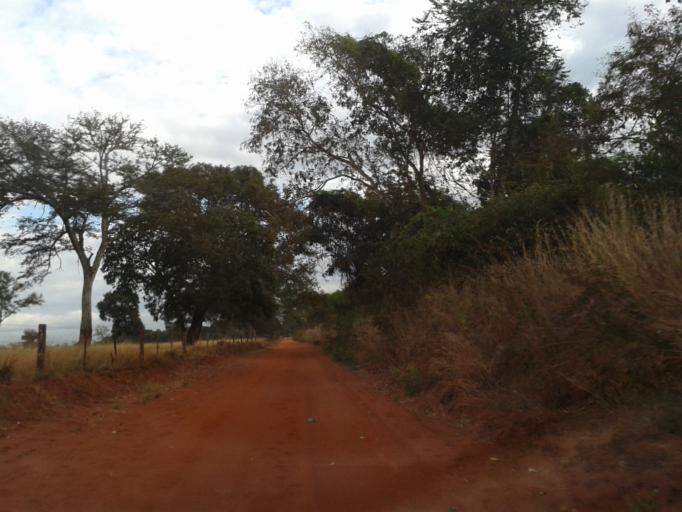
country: BR
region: Minas Gerais
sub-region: Santa Vitoria
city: Santa Vitoria
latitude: -18.7751
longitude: -50.1864
